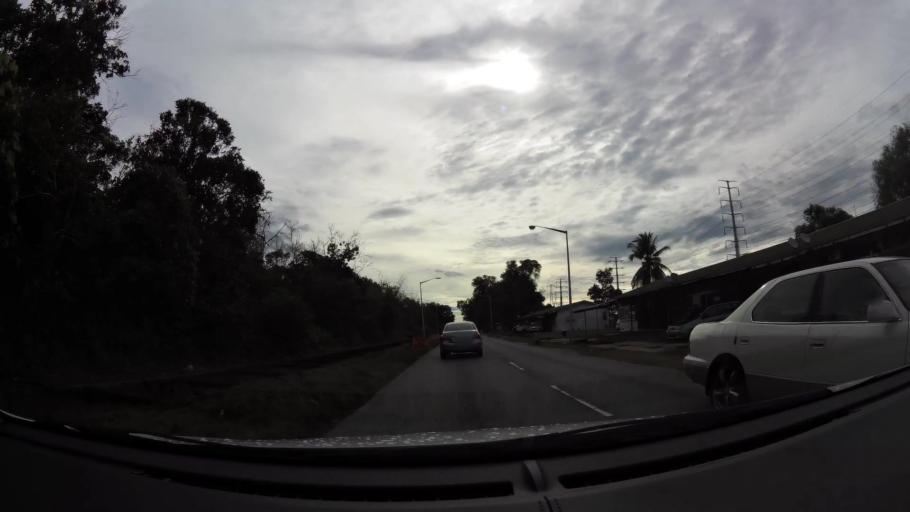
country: BN
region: Belait
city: Seria
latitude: 4.6153
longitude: 114.3405
